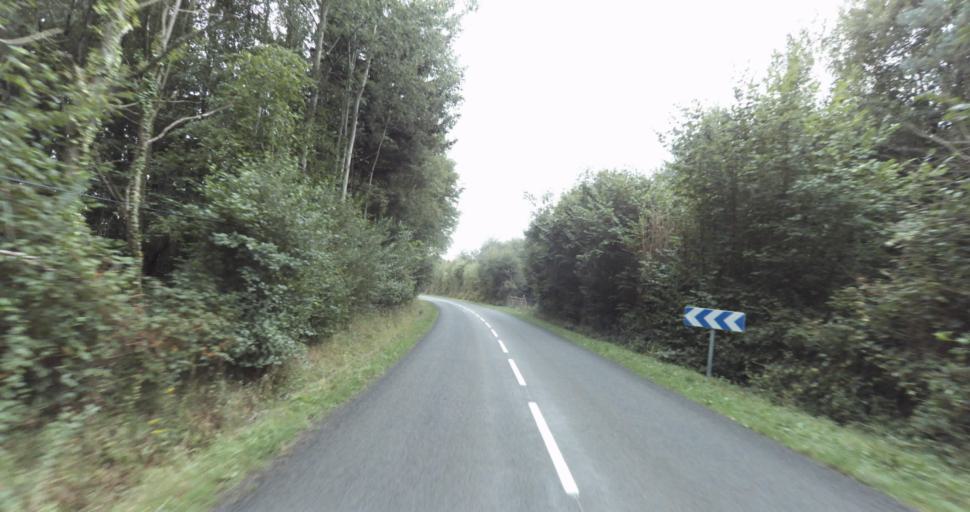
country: FR
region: Lower Normandy
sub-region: Departement de l'Orne
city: Sainte-Gauburge-Sainte-Colombe
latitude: 48.7513
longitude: 0.4359
